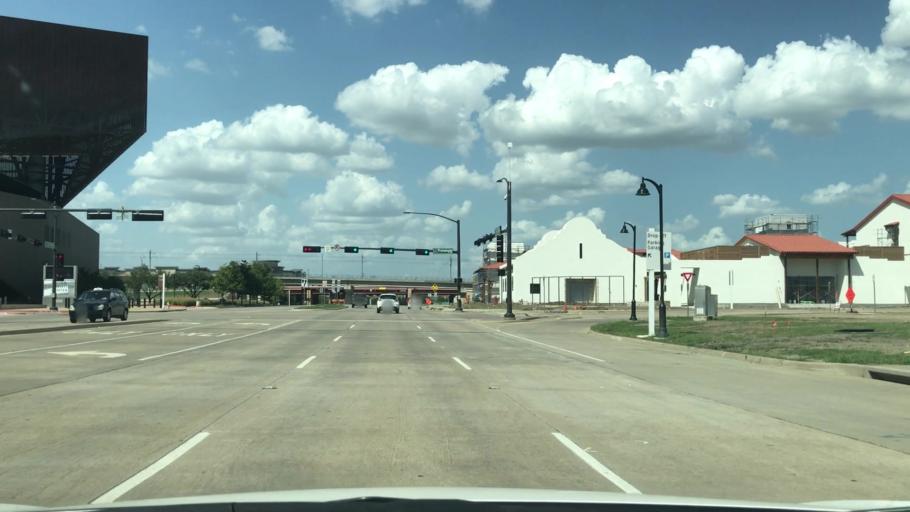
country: US
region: Texas
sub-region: Dallas County
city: Irving
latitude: 32.8765
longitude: -96.9428
